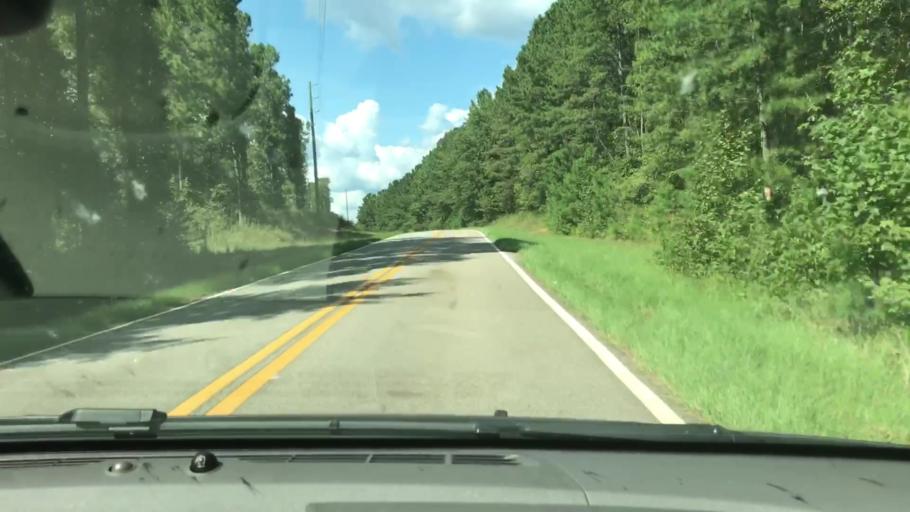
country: US
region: Georgia
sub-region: Troup County
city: La Grange
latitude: 33.1400
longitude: -85.1158
